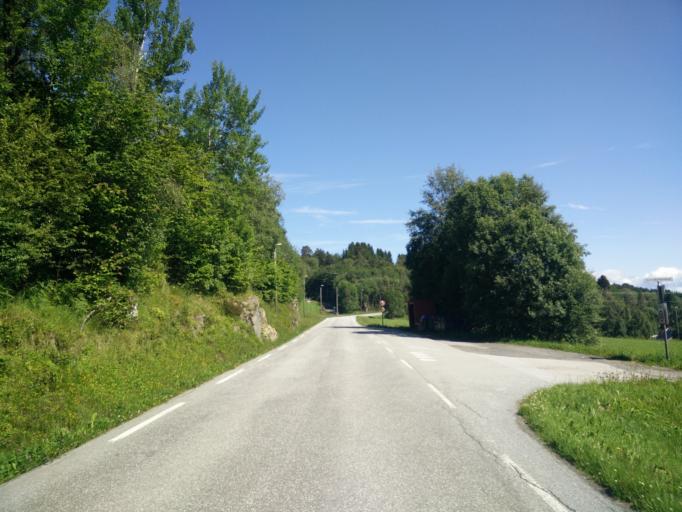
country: NO
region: More og Romsdal
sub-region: Kristiansund
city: Rensvik
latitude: 63.0483
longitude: 7.8581
